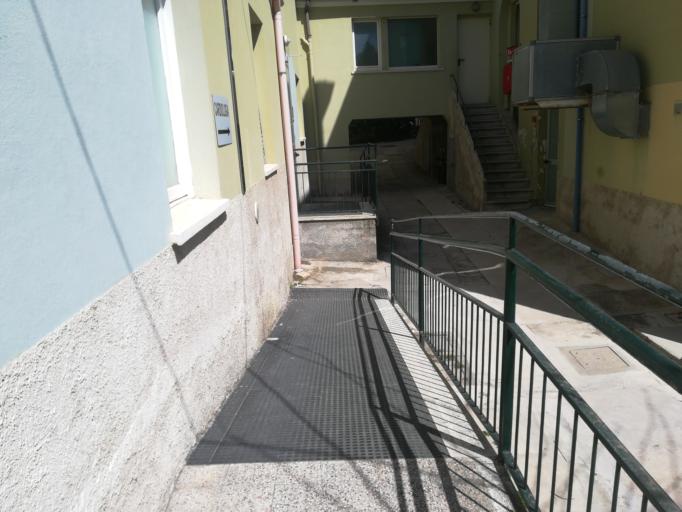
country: IT
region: The Marches
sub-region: Provincia di Macerata
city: Macerata
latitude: 43.2963
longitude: 13.4544
